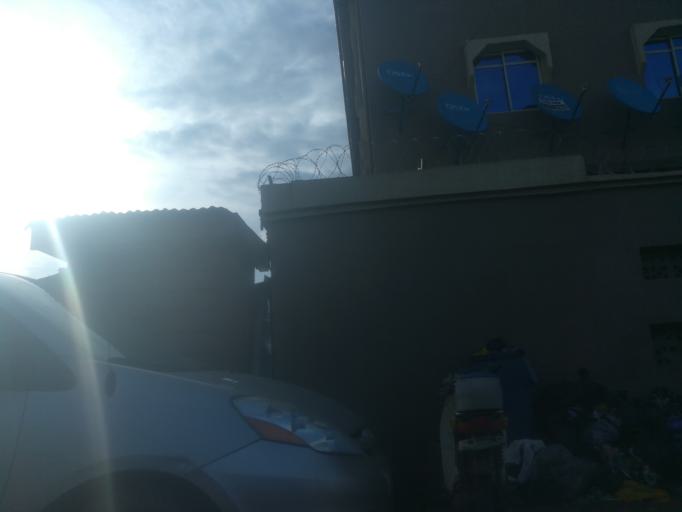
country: NG
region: Lagos
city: Somolu
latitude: 6.5419
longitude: 3.3856
